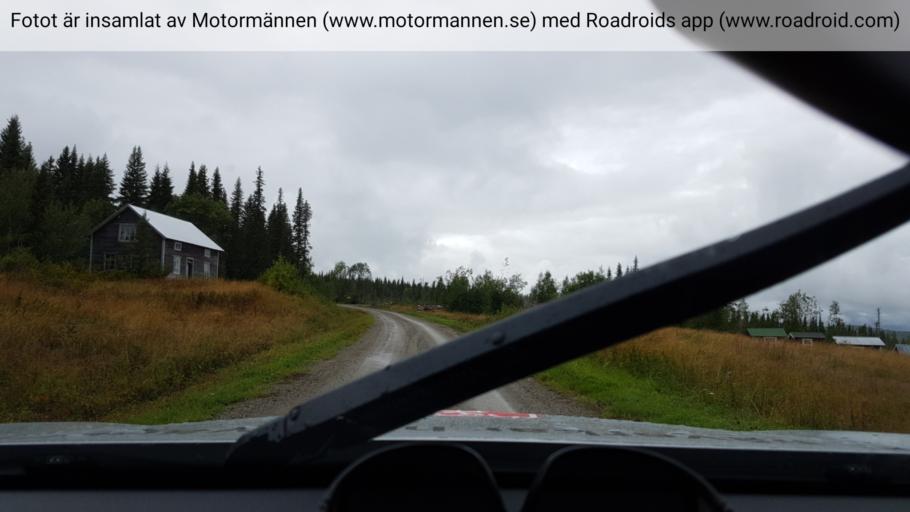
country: SE
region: Vaesterbotten
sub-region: Asele Kommun
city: Insjon
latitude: 64.8003
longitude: 17.4814
